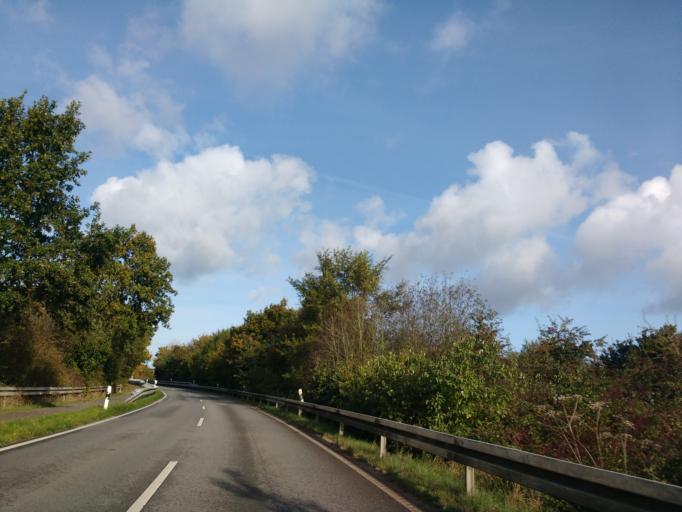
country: DE
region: Schleswig-Holstein
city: Altenkrempe
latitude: 54.1245
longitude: 10.8226
